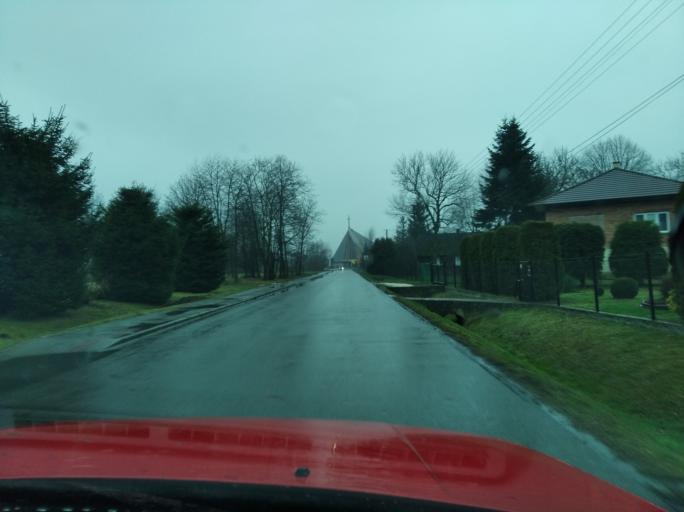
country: PL
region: Subcarpathian Voivodeship
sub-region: Powiat lancucki
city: Krzemienica
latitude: 50.0788
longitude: 22.1377
